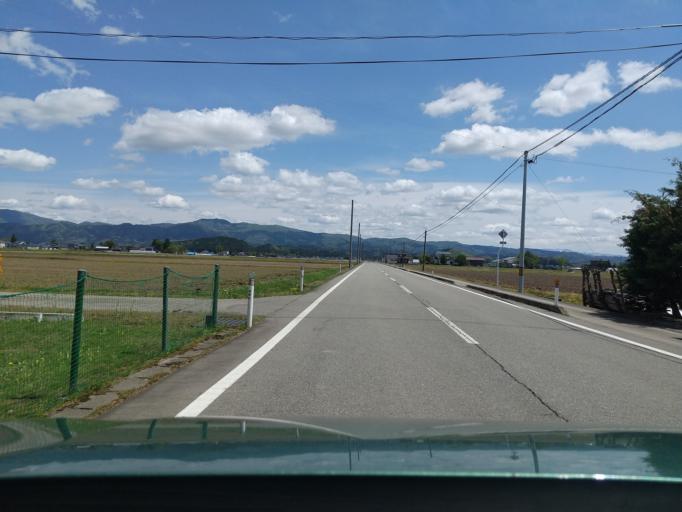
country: JP
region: Akita
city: Yokotemachi
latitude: 39.3835
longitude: 140.5178
